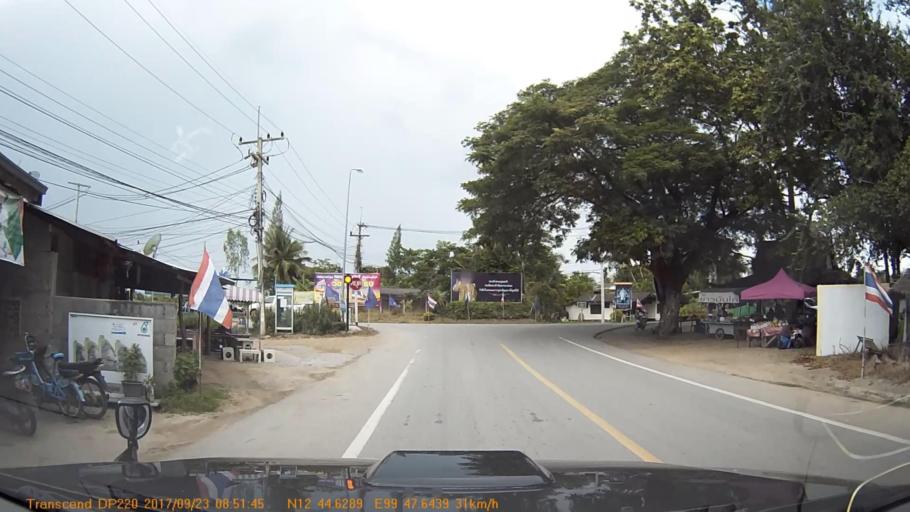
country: TH
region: Phetchaburi
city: Cha-am
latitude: 12.7435
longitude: 99.7945
